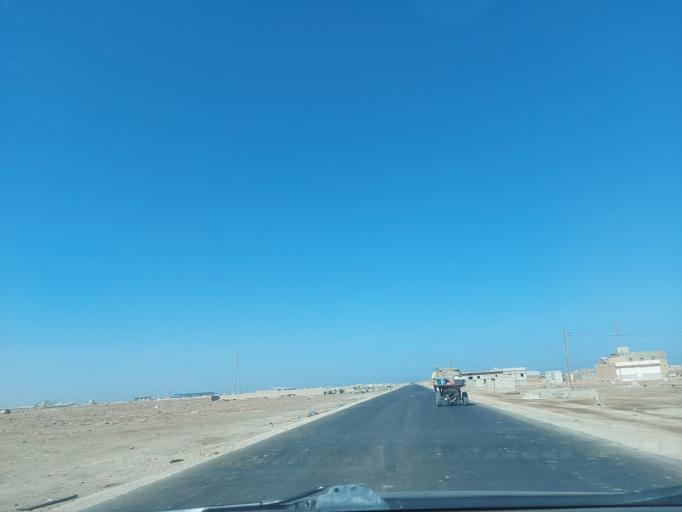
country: MR
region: Nouakchott
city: Nouakchott
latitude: 18.0604
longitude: -16.0081
